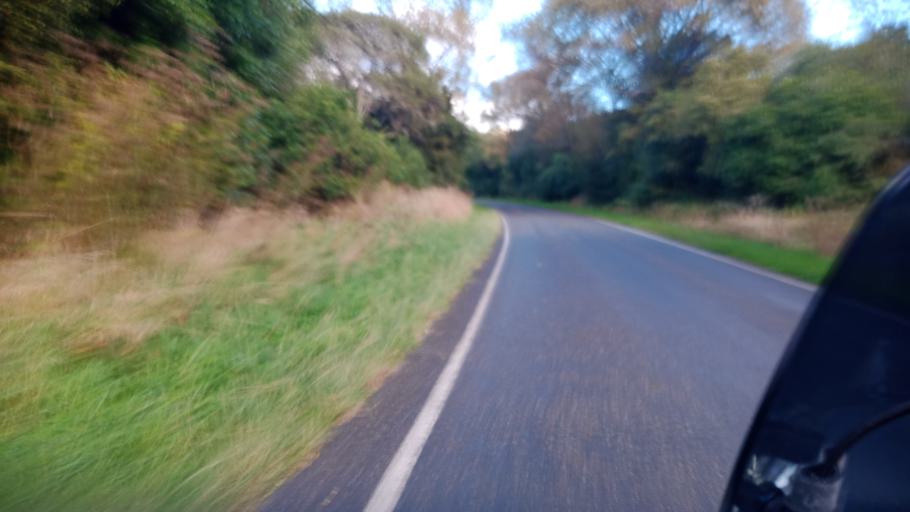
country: NZ
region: Gisborne
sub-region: Gisborne District
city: Gisborne
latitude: -38.5375
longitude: 177.5744
